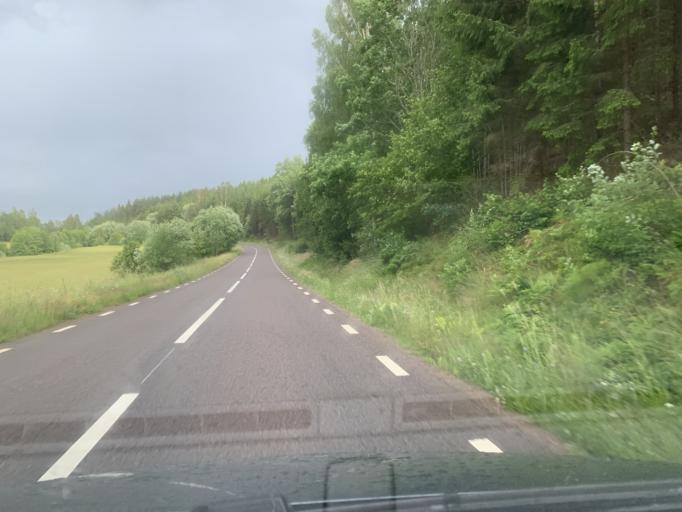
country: SE
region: Kalmar
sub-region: Vasterviks Kommun
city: Overum
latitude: 58.0184
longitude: 16.1500
